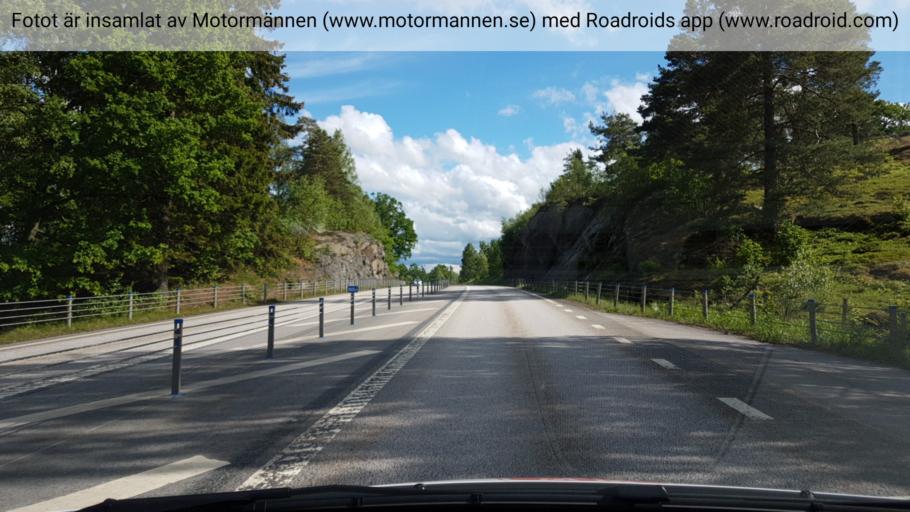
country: SE
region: Kalmar
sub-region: Vasterviks Kommun
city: Gamleby
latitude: 57.8855
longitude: 16.3876
